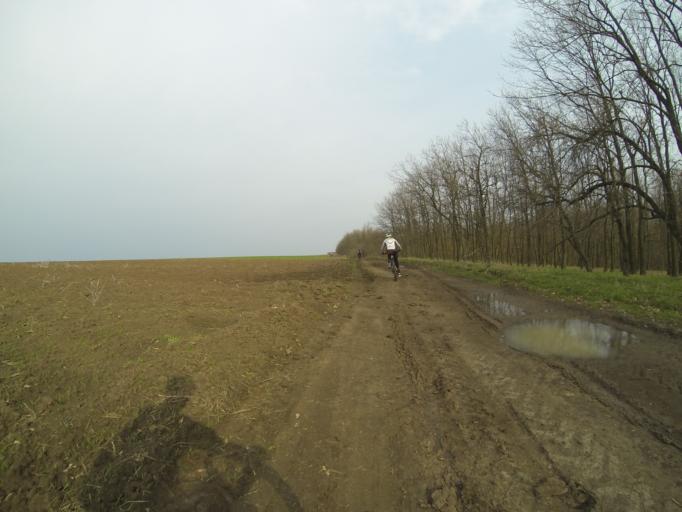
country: RO
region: Dolj
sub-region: Comuna Bucovat
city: Bucovat
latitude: 44.2597
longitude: 23.6970
